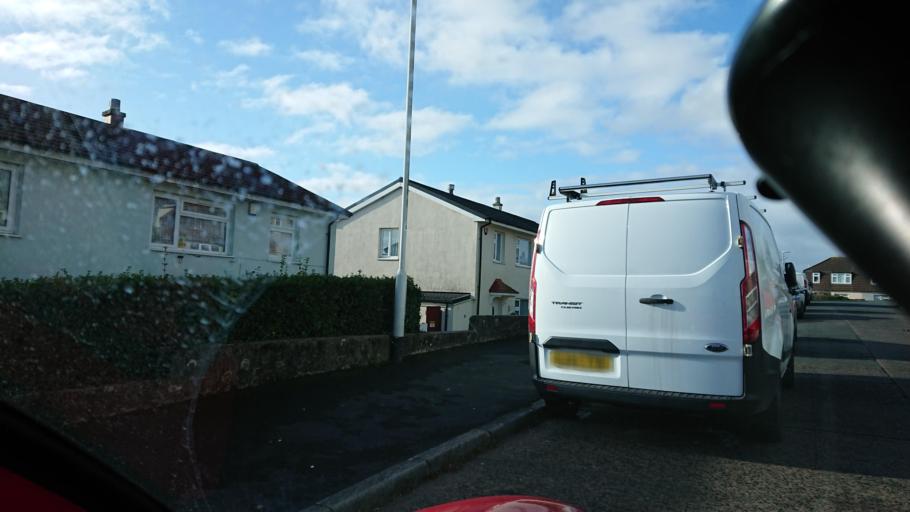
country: GB
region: England
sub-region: Plymouth
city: Plymouth
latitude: 50.4084
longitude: -4.1609
